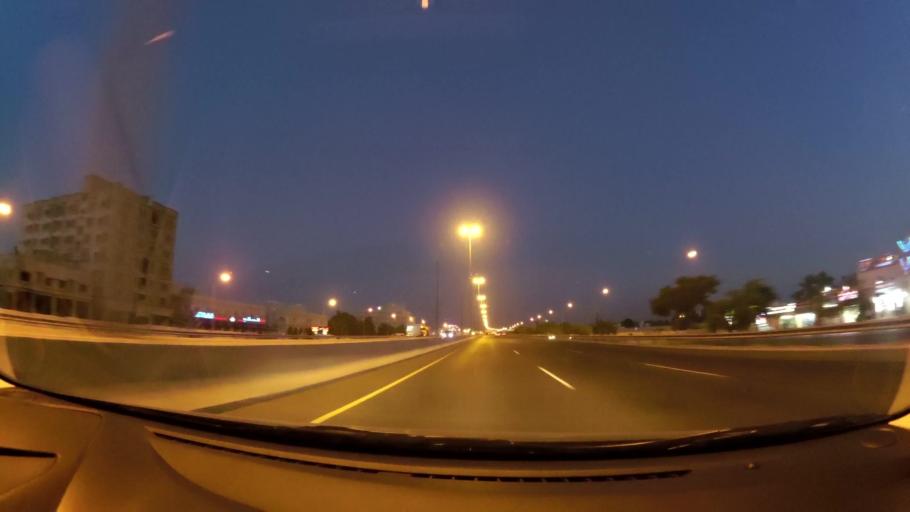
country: OM
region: Muhafazat Masqat
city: As Sib al Jadidah
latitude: 23.6383
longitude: 58.2263
